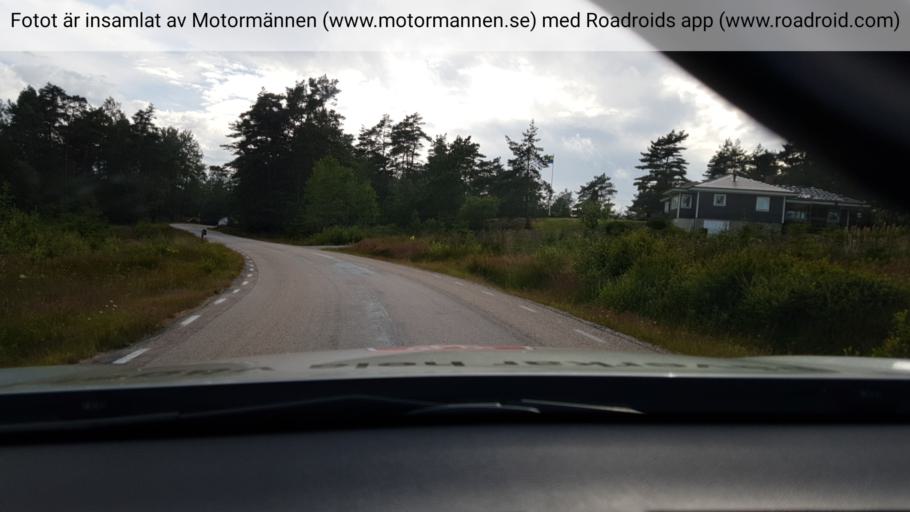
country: SE
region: Vaestra Goetaland
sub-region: Orust
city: Henan
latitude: 58.1621
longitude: 11.6881
